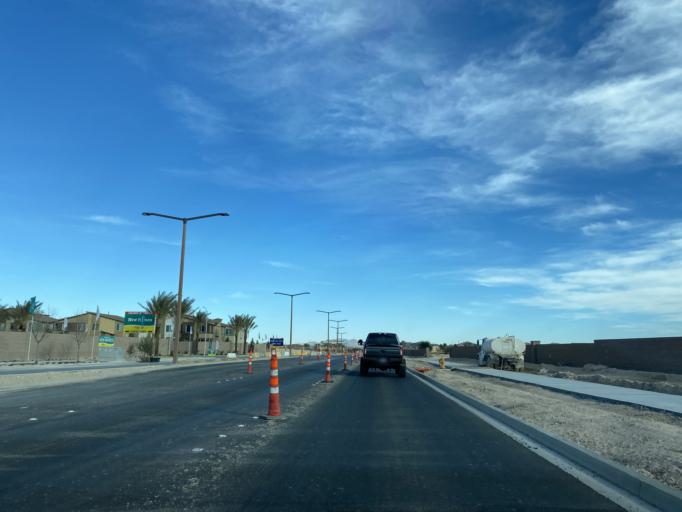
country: US
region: Nevada
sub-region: Clark County
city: North Las Vegas
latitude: 36.2912
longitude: -115.2016
